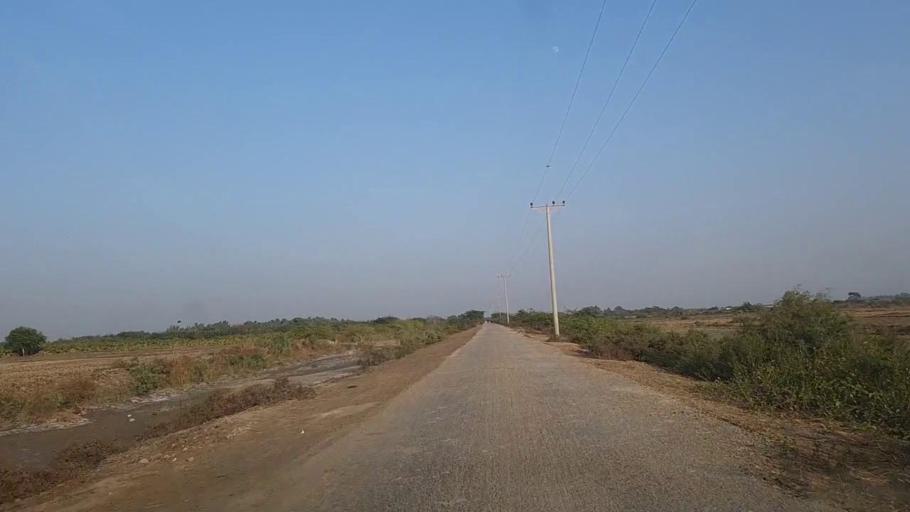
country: PK
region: Sindh
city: Keti Bandar
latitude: 24.2805
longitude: 67.6188
